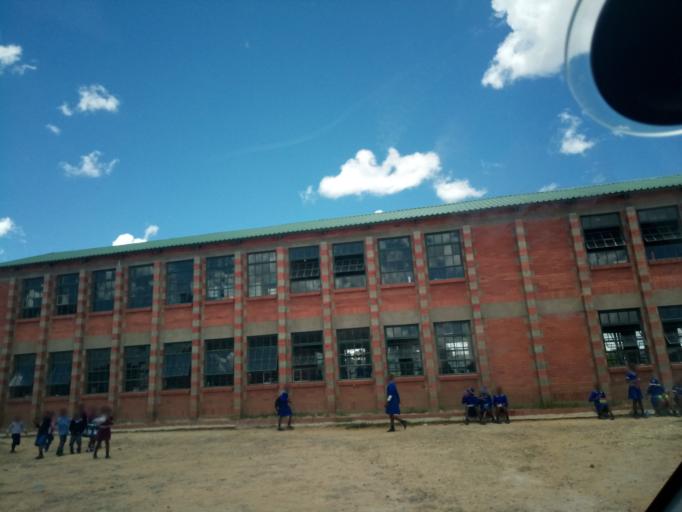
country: LS
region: Maseru
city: Maseru
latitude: -29.3537
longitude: 27.5455
